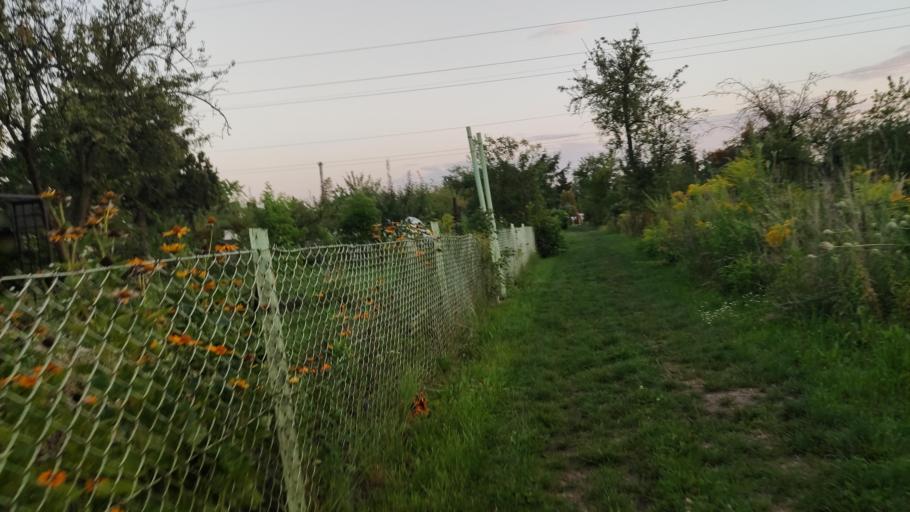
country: PL
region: Lower Silesian Voivodeship
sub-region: Powiat wroclawski
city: Wroclaw
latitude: 51.1024
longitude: 16.9813
